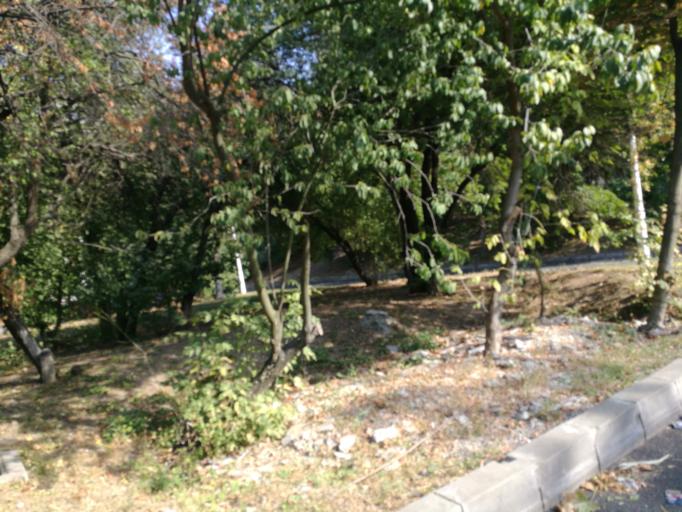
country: RO
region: Bucuresti
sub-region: Municipiul Bucuresti
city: Bucuresti
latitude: 44.4816
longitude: 26.0687
